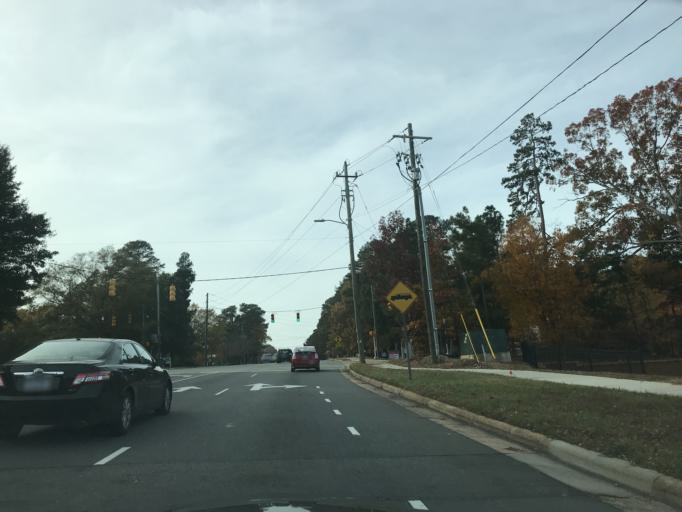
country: US
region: North Carolina
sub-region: Wake County
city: West Raleigh
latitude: 35.8155
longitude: -78.6994
